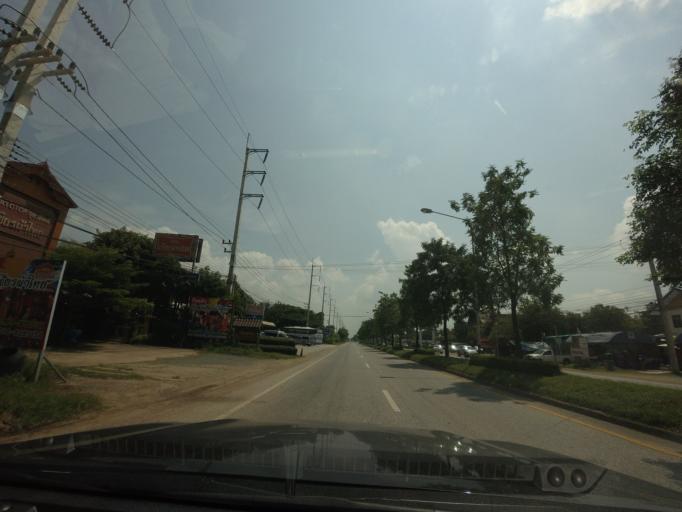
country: TH
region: Uttaradit
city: Uttaradit
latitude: 17.5942
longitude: 100.1302
